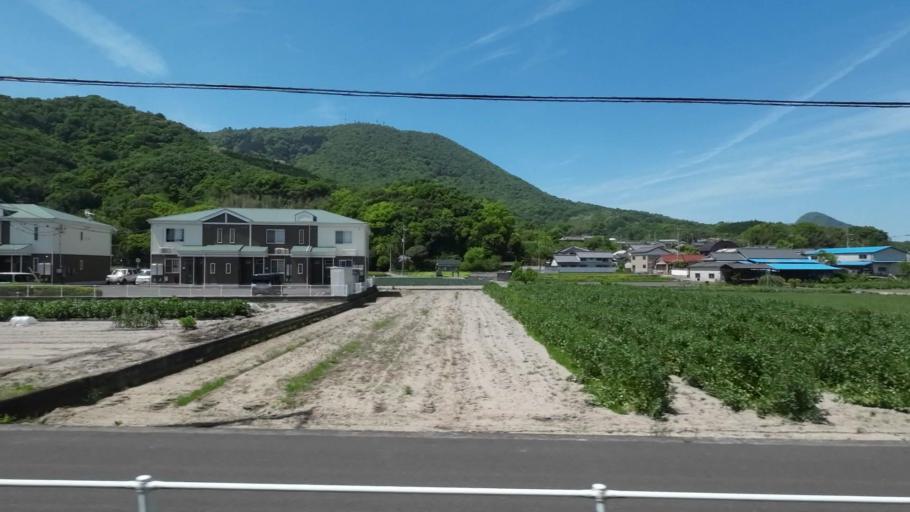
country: JP
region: Kagawa
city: Marugame
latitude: 34.2091
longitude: 133.8046
